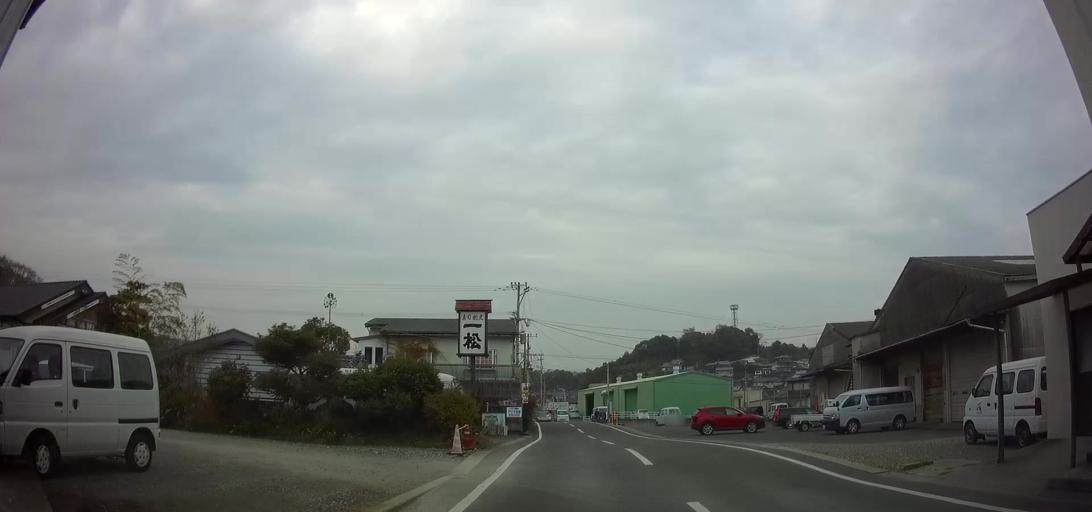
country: JP
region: Kumamoto
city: Hondo
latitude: 32.6323
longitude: 130.2470
